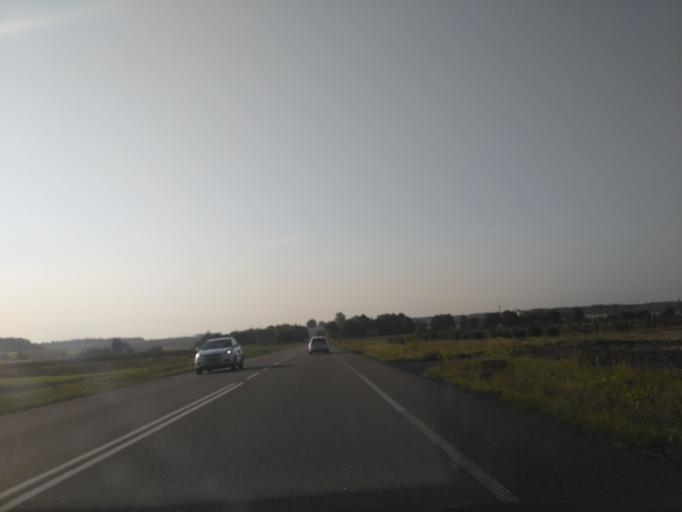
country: PL
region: Lublin Voivodeship
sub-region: Powiat janowski
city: Modliborzyce
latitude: 50.7361
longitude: 22.3529
